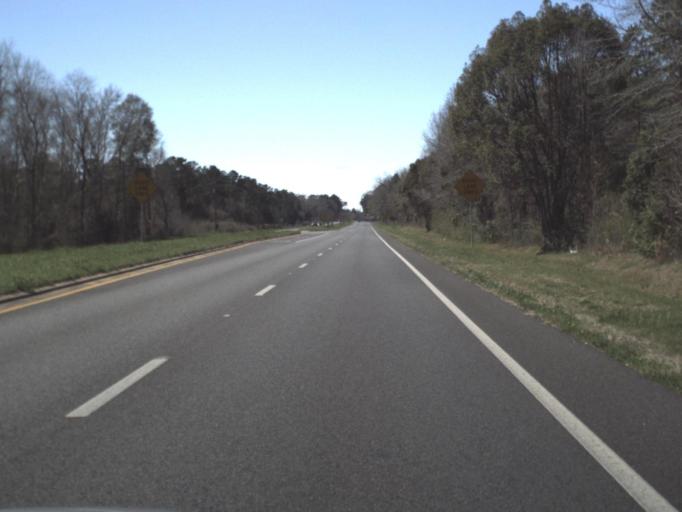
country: US
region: Florida
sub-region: Gadsden County
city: Gretna
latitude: 30.5906
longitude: -84.6335
